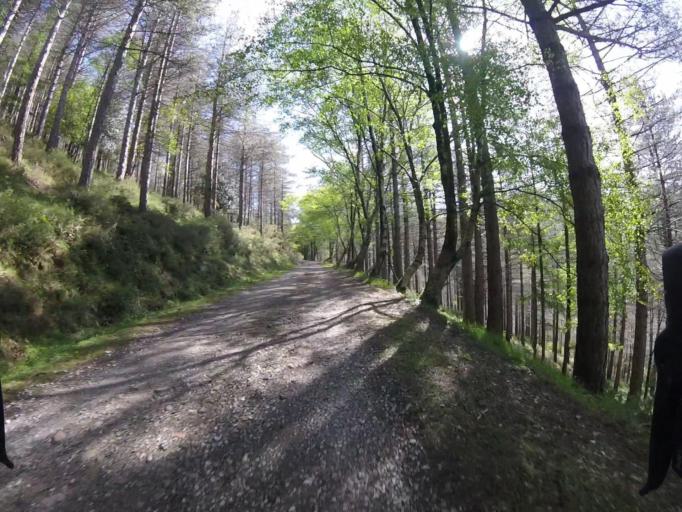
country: ES
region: Basque Country
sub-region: Provincia de Guipuzcoa
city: Andoain
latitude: 43.1943
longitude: -1.9866
